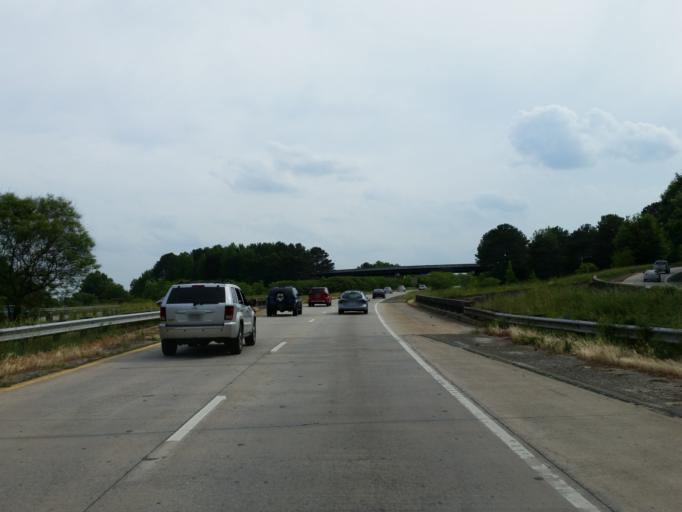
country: US
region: Georgia
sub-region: Cobb County
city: Marietta
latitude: 33.9882
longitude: -84.5385
